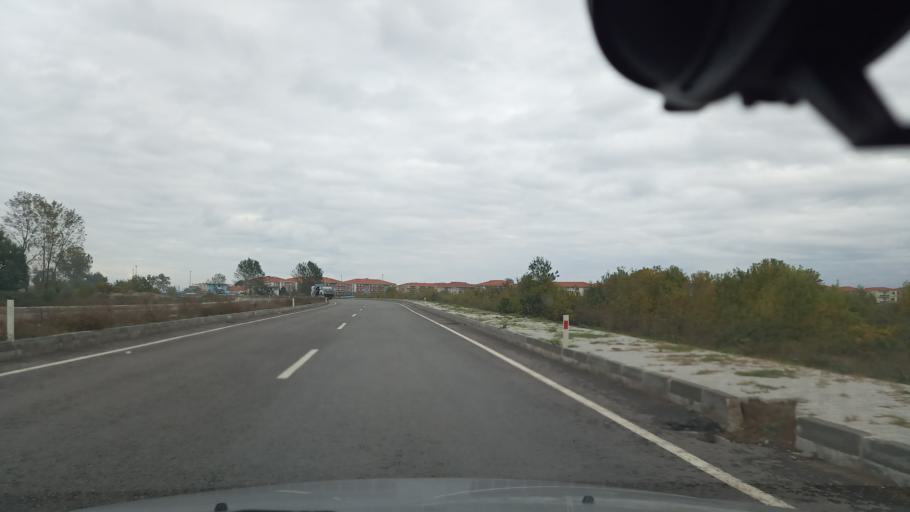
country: TR
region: Sakarya
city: Karasu
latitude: 41.1137
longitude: 30.6633
